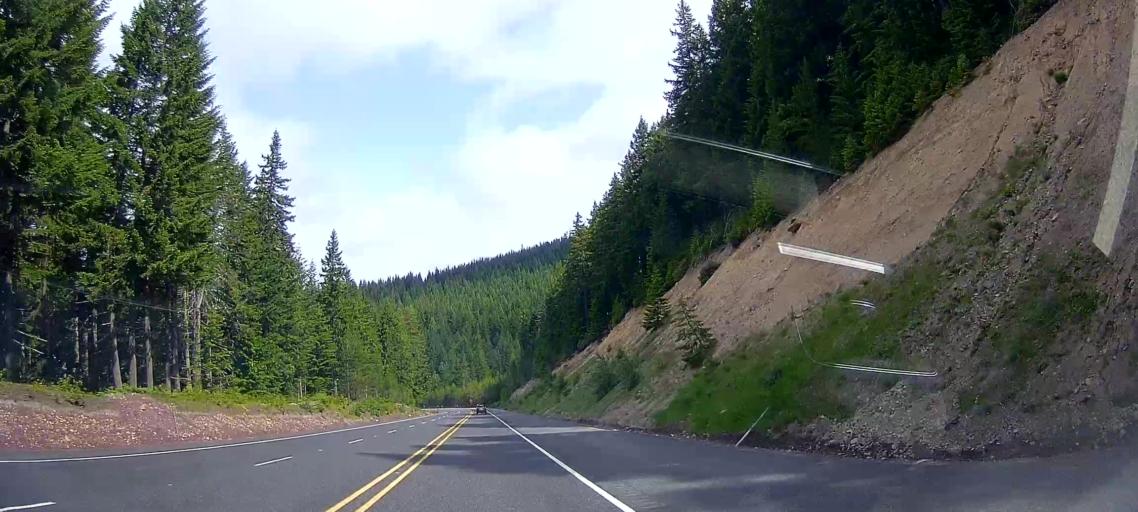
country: US
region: Oregon
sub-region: Clackamas County
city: Mount Hood Village
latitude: 45.2383
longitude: -121.6985
